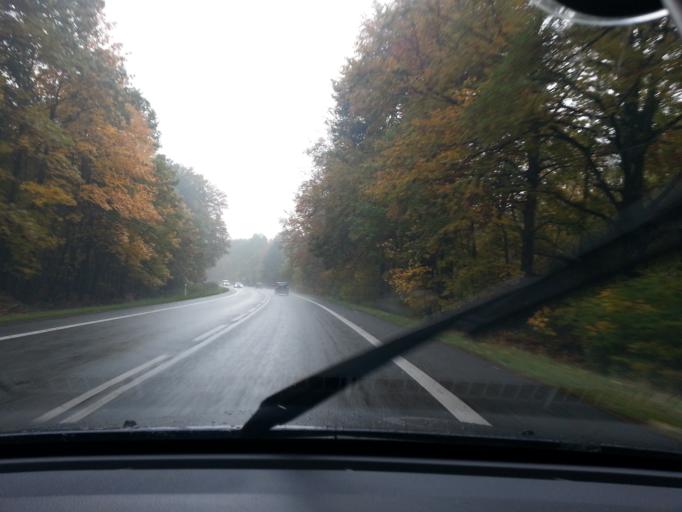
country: PL
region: Silesian Voivodeship
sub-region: Powiat gliwicki
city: Pilchowice
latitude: 50.1770
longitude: 18.5462
